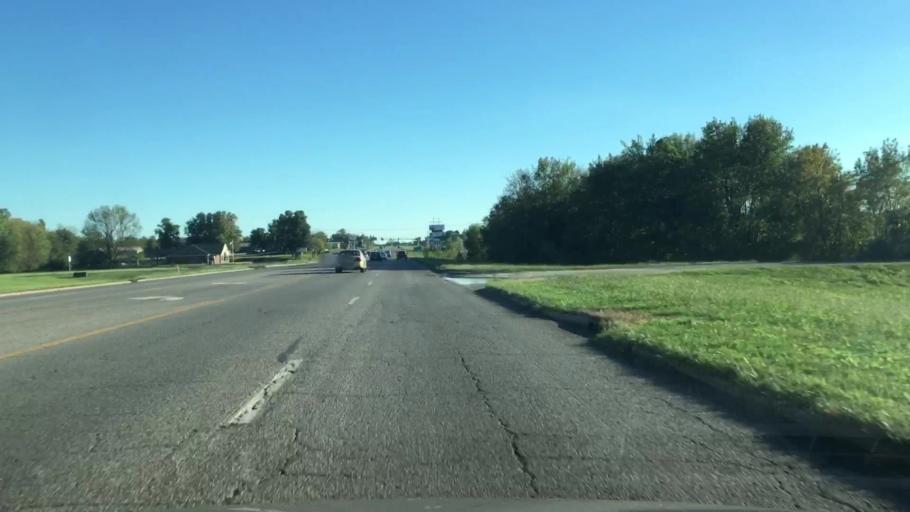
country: US
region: Oklahoma
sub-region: Cherokee County
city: Park Hill
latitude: 35.8746
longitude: -94.9763
